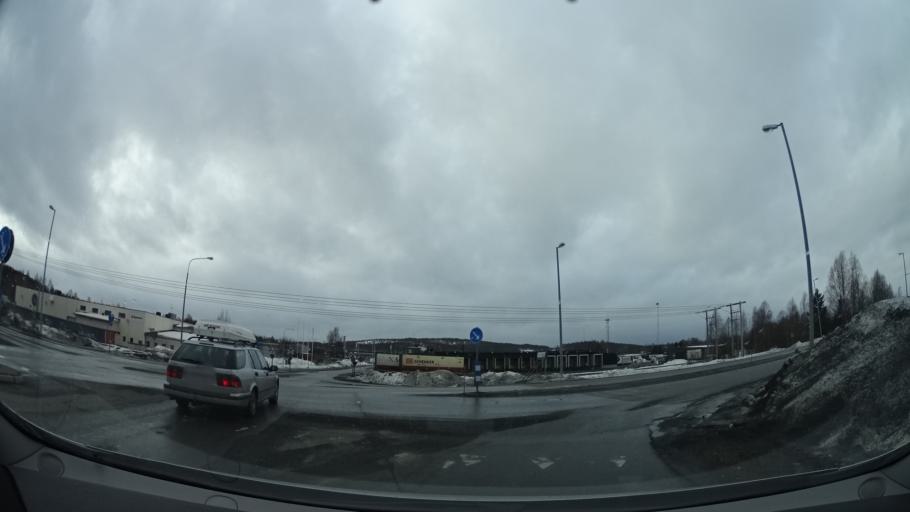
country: SE
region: Vaesterbotten
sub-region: Skelleftea Kommun
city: Soedra Bergsbyn
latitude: 64.7478
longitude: 21.0354
